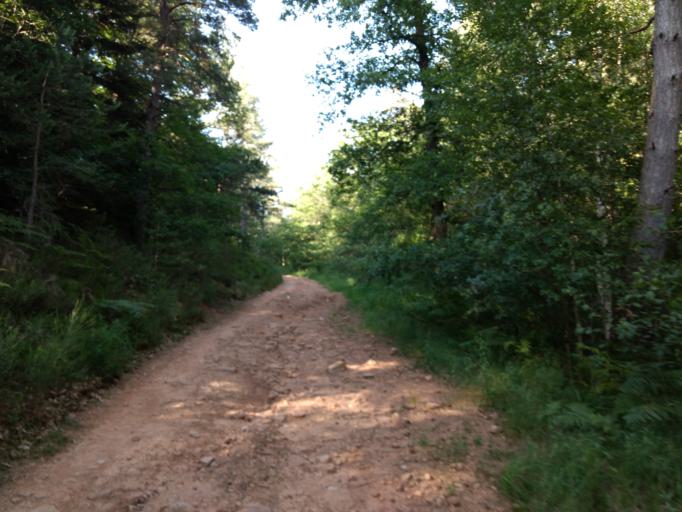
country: FR
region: Midi-Pyrenees
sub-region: Departement de l'Aveyron
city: La Loubiere
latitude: 44.3585
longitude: 2.7033
